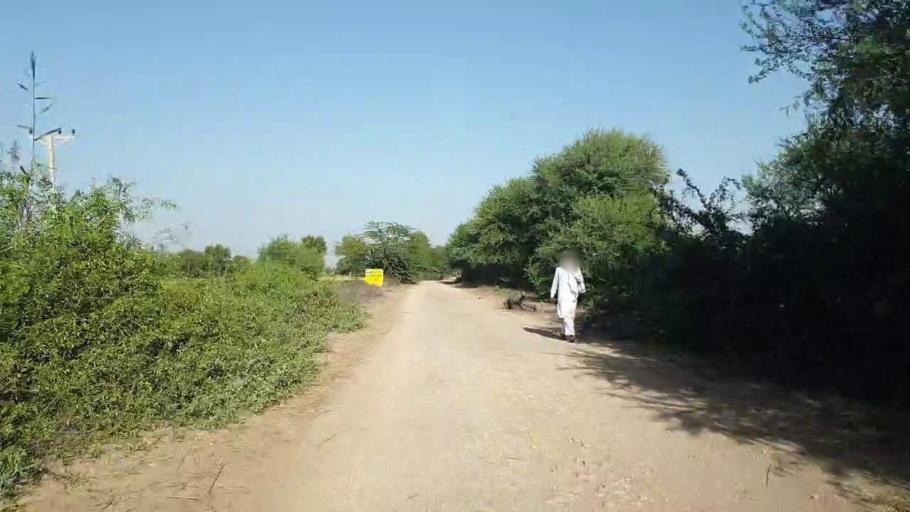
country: PK
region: Sindh
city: Badin
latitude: 24.6017
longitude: 68.9165
